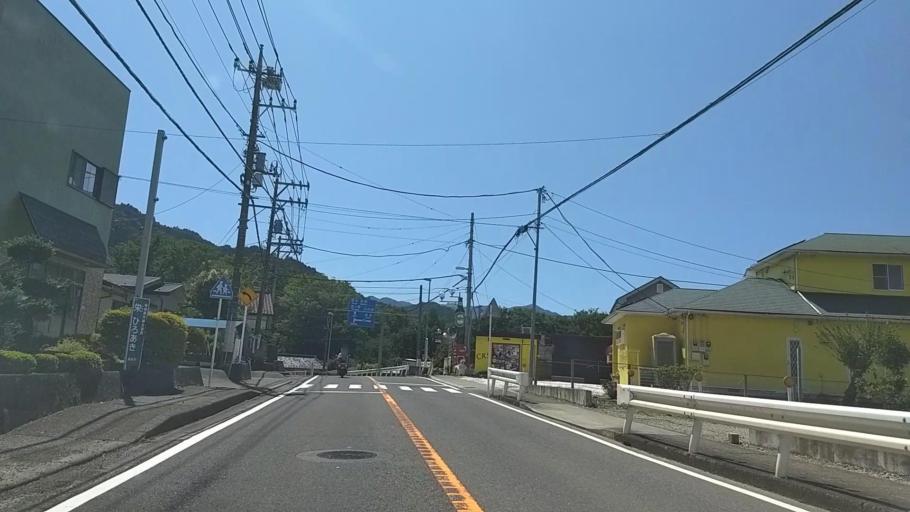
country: JP
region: Tokyo
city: Hachioji
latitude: 35.5841
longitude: 139.2302
